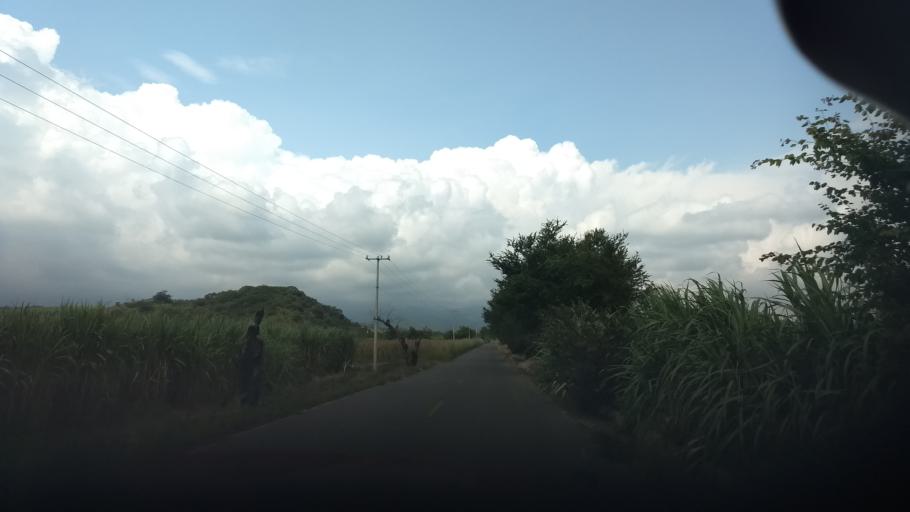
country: MX
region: Jalisco
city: Tonila
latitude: 19.4213
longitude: -103.4898
